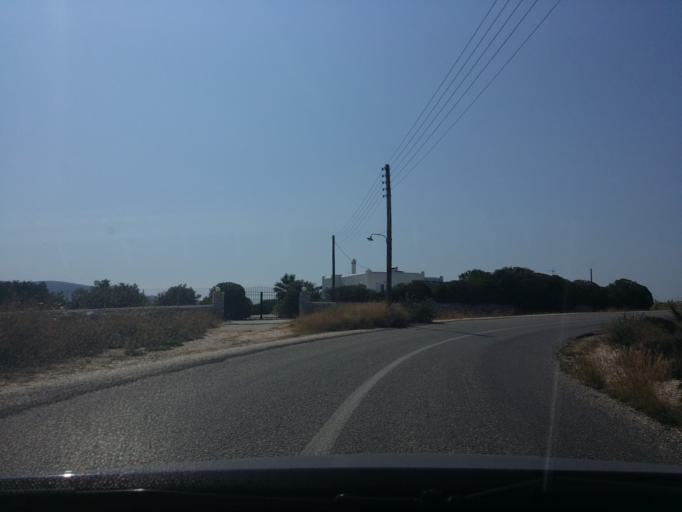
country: GR
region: South Aegean
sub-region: Nomos Kykladon
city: Antiparos
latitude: 37.0325
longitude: 25.1105
